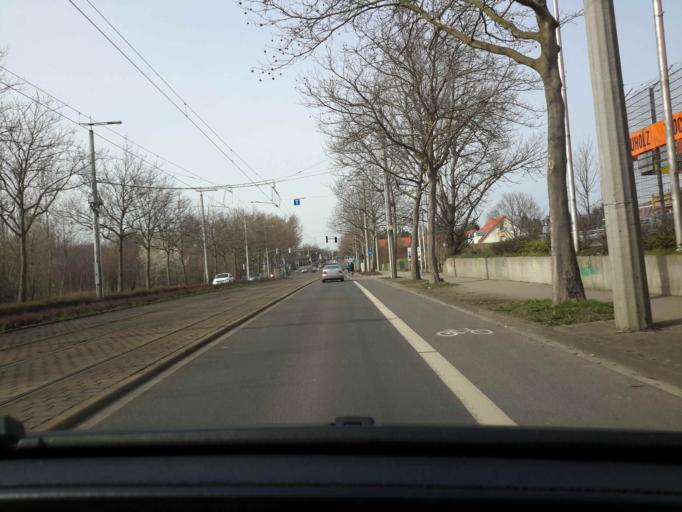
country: DE
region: Saxony
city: Leipzig
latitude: 51.3813
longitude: 12.3836
